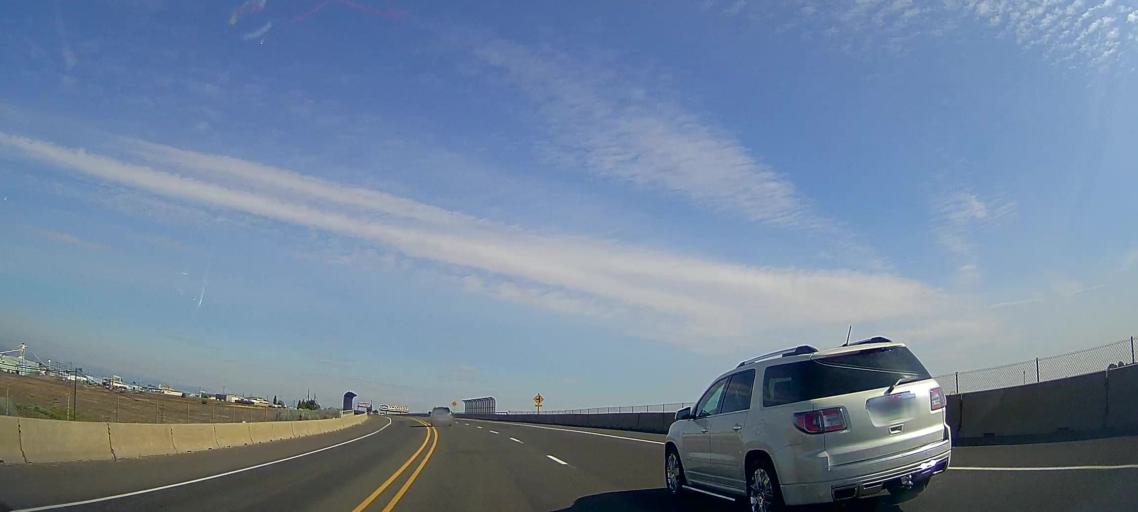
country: US
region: Oregon
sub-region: Jefferson County
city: Madras
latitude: 44.6548
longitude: -121.1288
